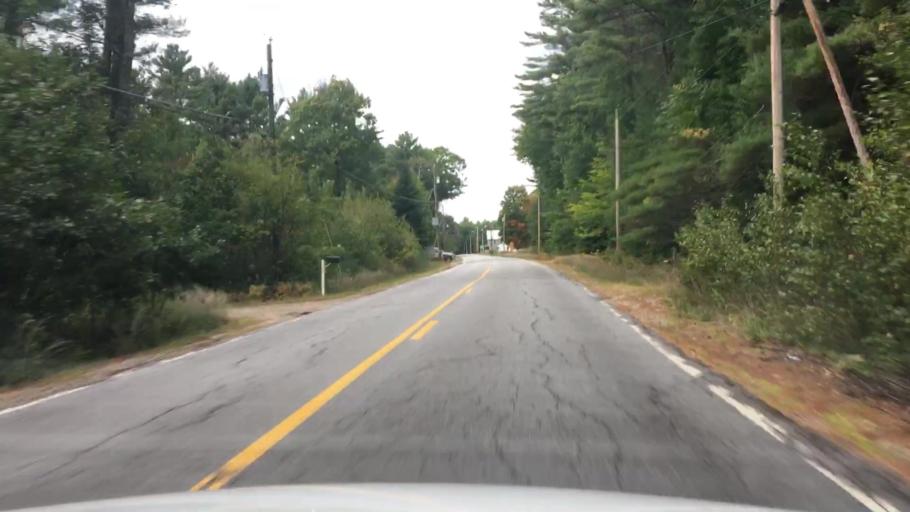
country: US
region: New Hampshire
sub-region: Carroll County
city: Effingham
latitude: 43.7088
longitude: -70.9820
